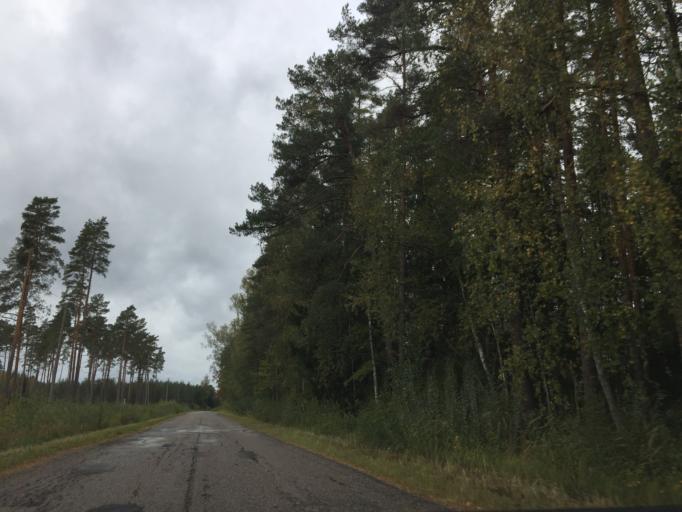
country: LV
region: Olaine
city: Olaine
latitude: 56.7645
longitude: 23.8897
